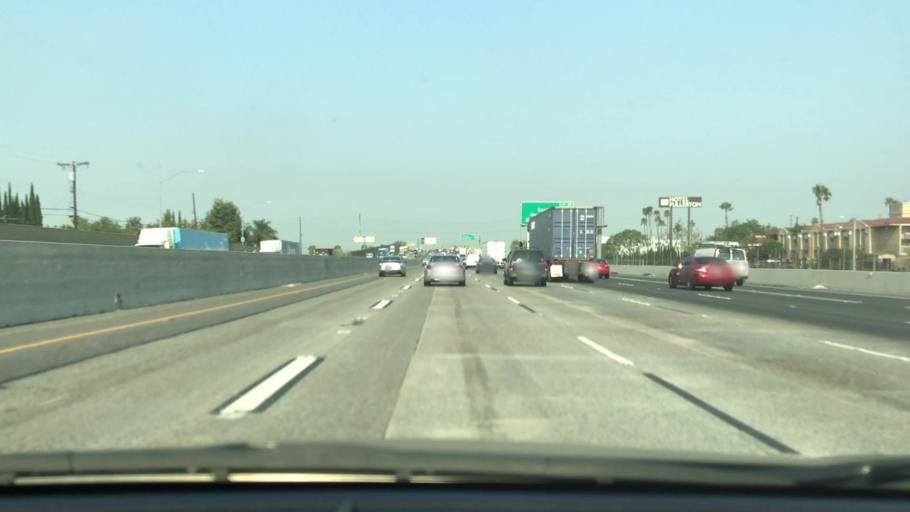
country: US
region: California
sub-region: Orange County
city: Anaheim
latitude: 33.8544
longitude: -117.9031
